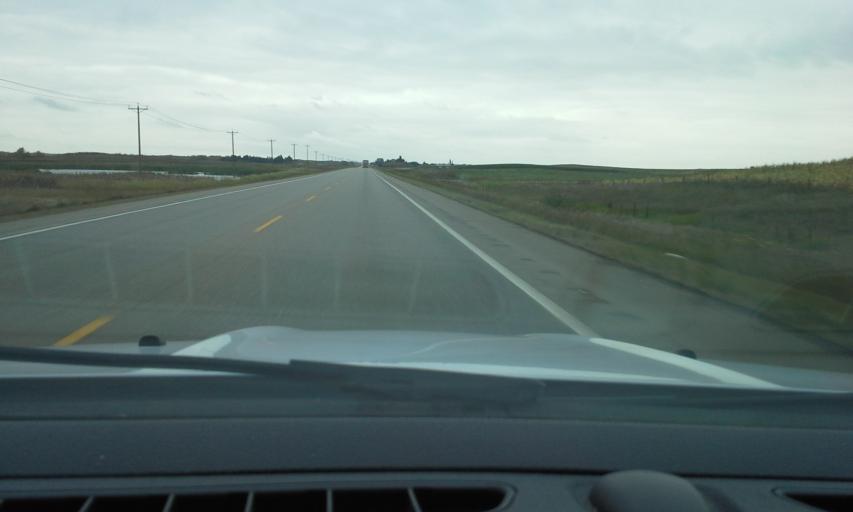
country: CA
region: Saskatchewan
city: Lloydminster
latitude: 53.2780
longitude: -109.8761
